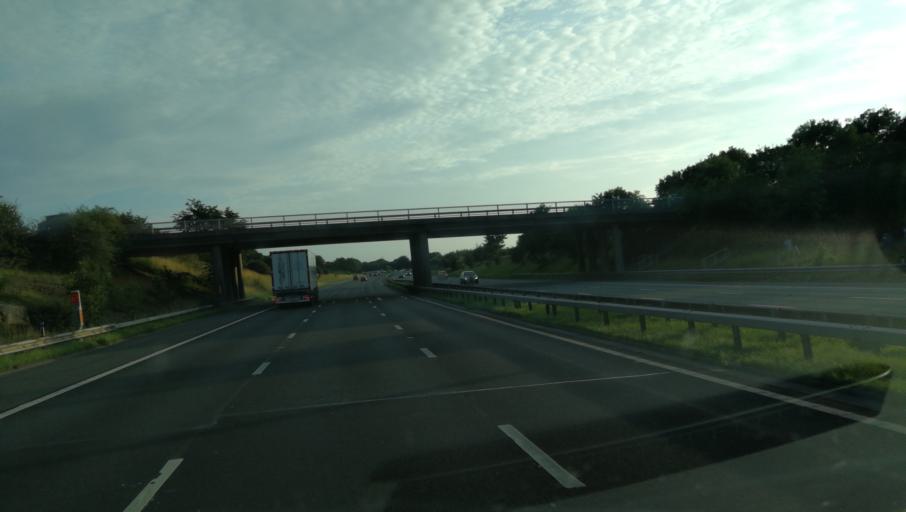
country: GB
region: England
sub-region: Lancashire
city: Carnforth
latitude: 54.1288
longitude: -2.7494
